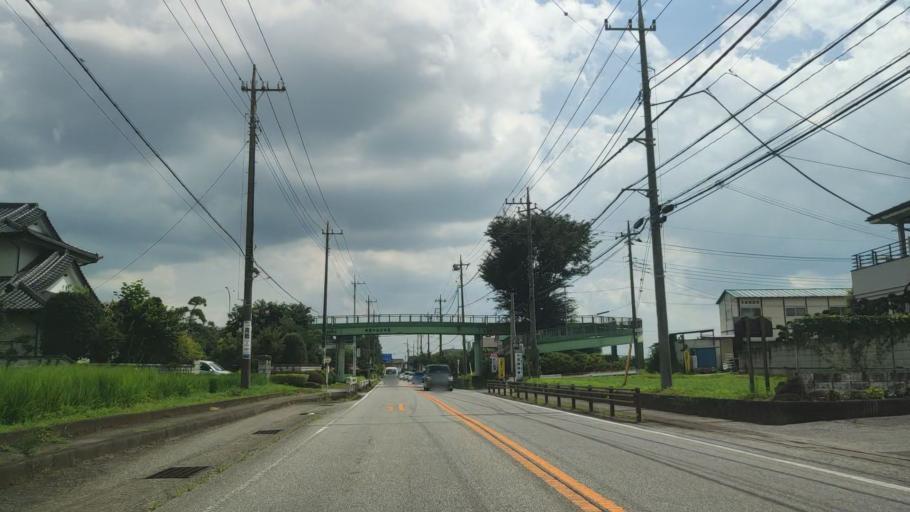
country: JP
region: Tochigi
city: Utsunomiya-shi
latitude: 36.6552
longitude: 139.8411
